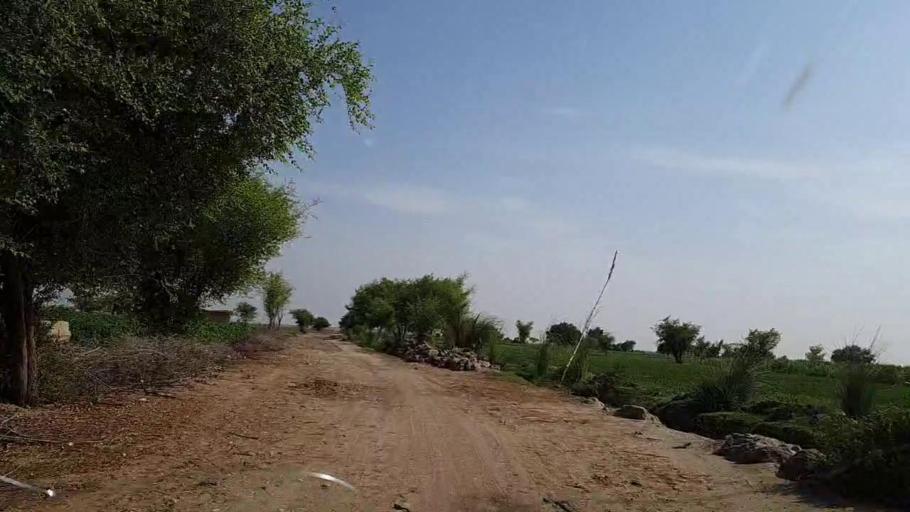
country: PK
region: Sindh
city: Khanpur
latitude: 27.6924
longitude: 69.3672
